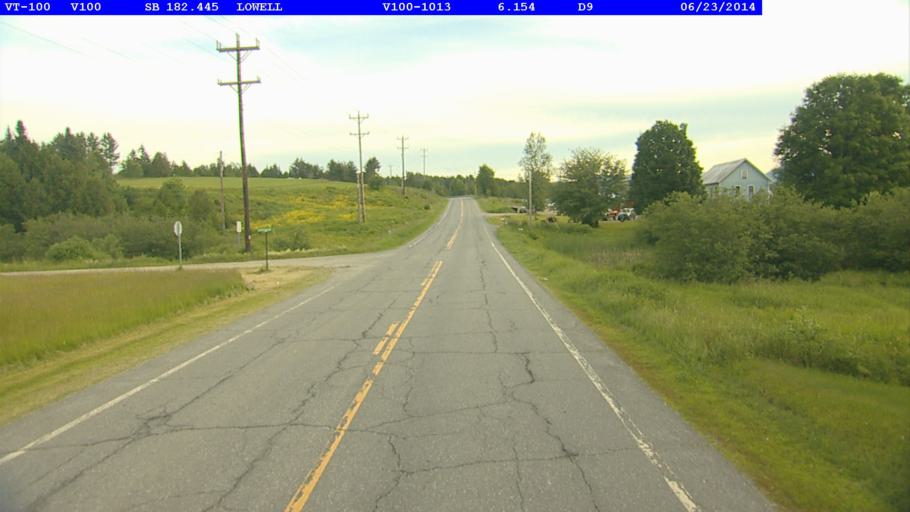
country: US
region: Vermont
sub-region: Orleans County
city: Newport
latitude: 44.8234
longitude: -72.4385
